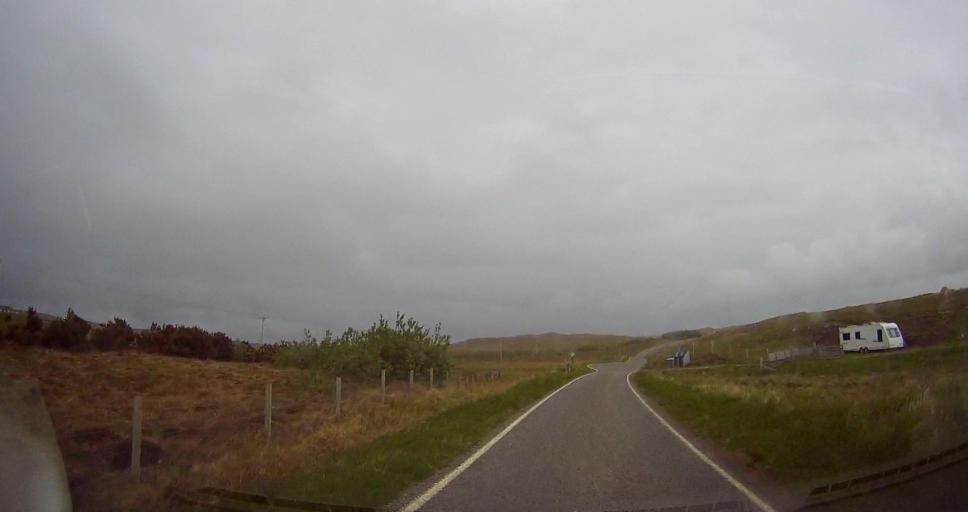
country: GB
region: Scotland
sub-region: Shetland Islands
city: Sandwick
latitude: 60.2312
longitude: -1.5597
